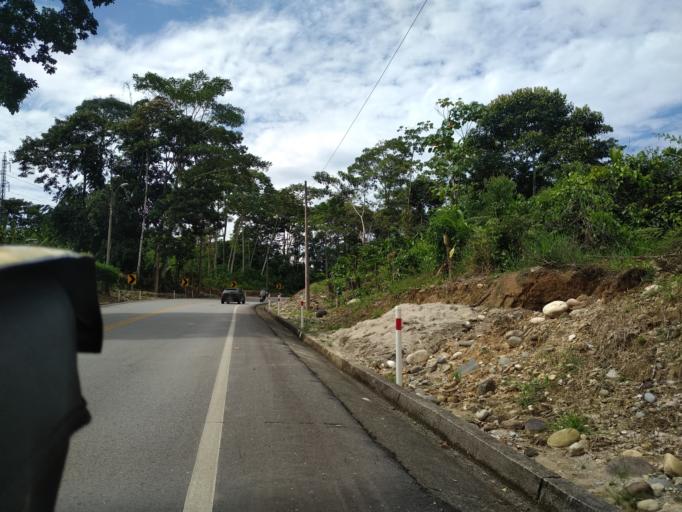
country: EC
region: Napo
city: Tena
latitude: -1.1351
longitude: -77.8319
